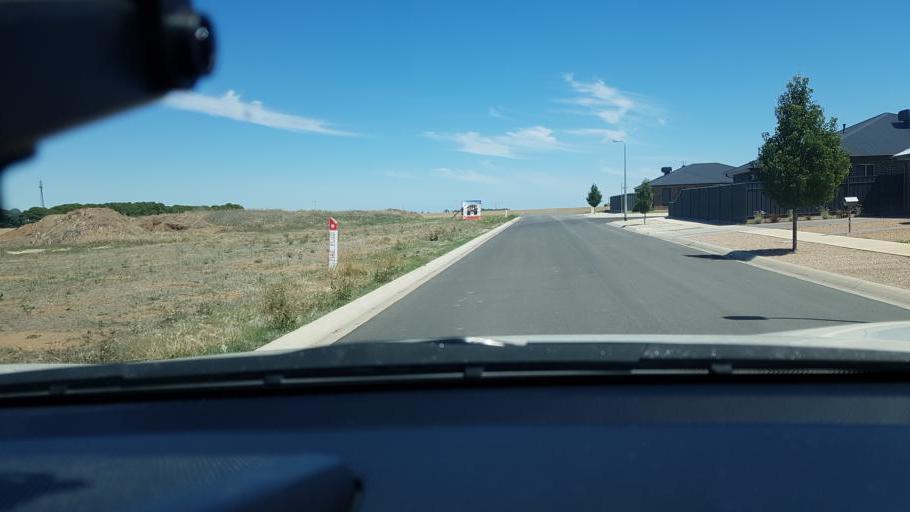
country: AU
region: Victoria
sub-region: Horsham
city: Horsham
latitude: -36.7159
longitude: 142.1776
